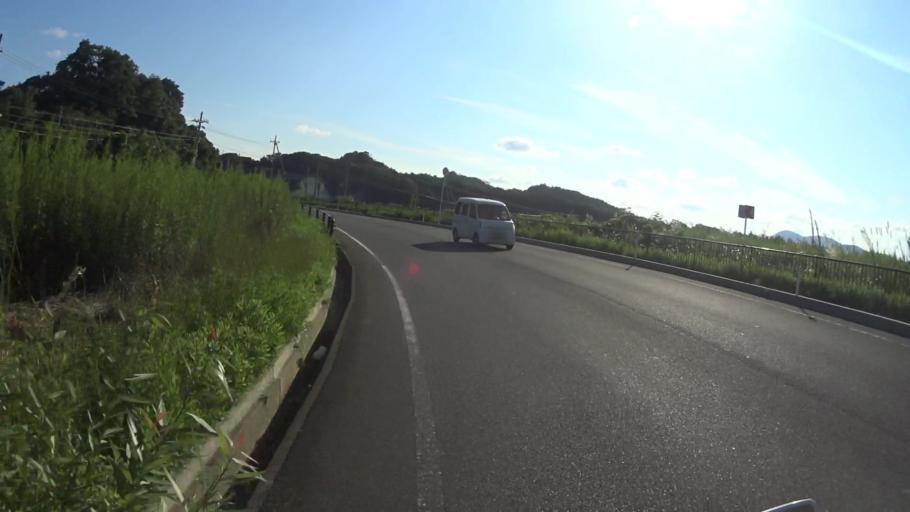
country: JP
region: Hyogo
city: Toyooka
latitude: 35.6445
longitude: 134.9453
